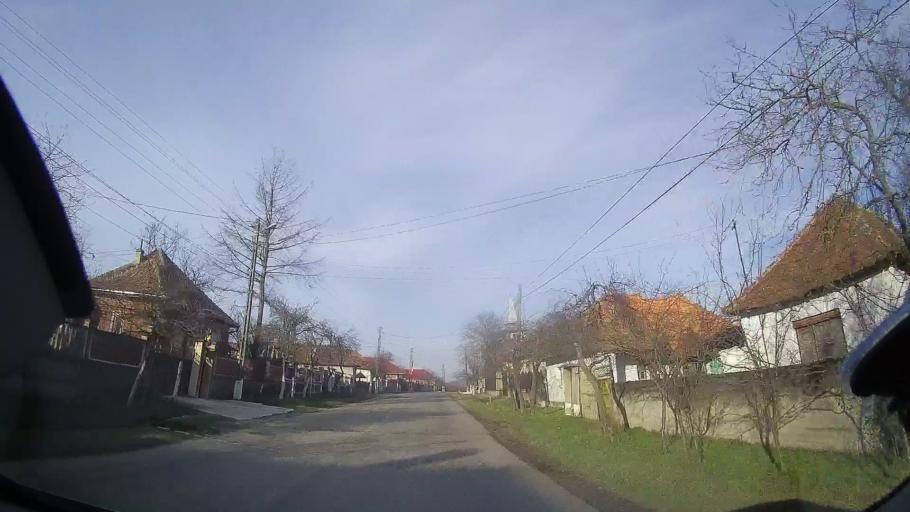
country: RO
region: Bihor
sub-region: Comuna Spinus
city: Spinus
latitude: 47.1733
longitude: 22.2183
